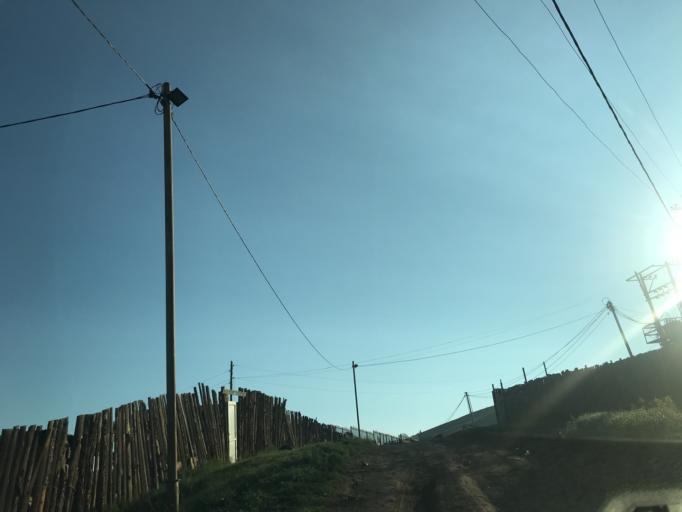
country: MN
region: Ulaanbaatar
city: Ulaanbaatar
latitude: 47.9905
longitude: 106.9649
